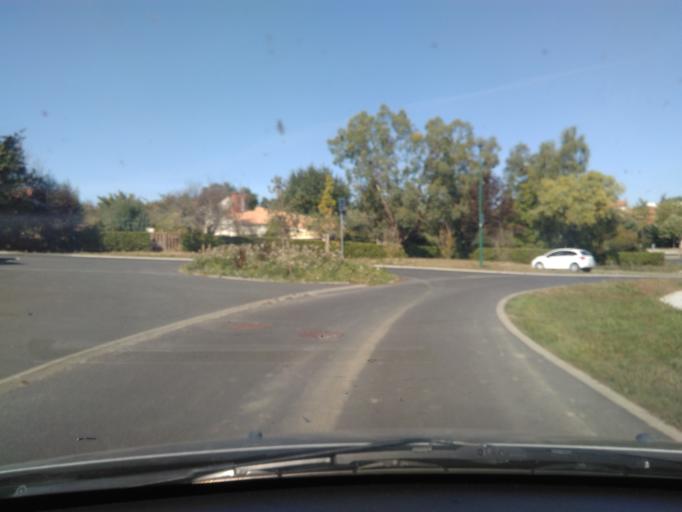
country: FR
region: Pays de la Loire
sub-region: Departement de la Vendee
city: Mouilleron-le-Captif
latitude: 46.7165
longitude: -1.4596
